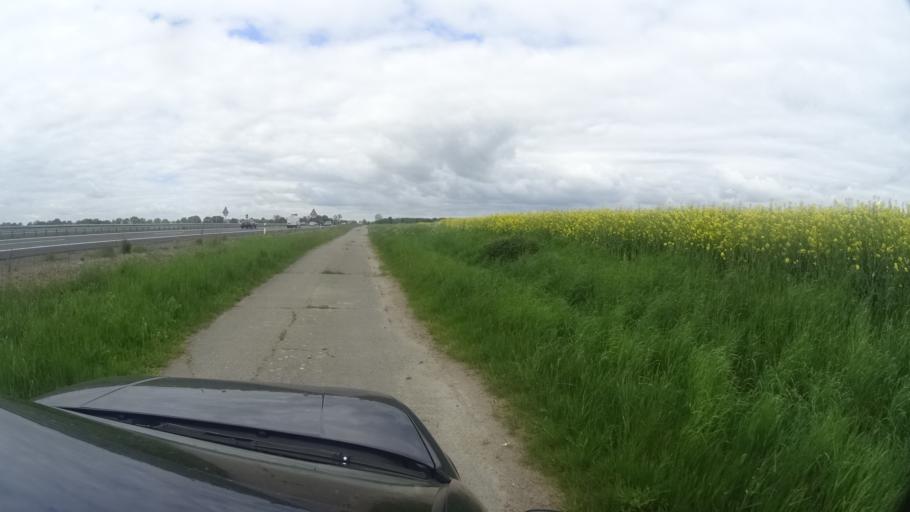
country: DE
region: Brandenburg
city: Dabergotz
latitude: 52.8741
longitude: 12.7605
